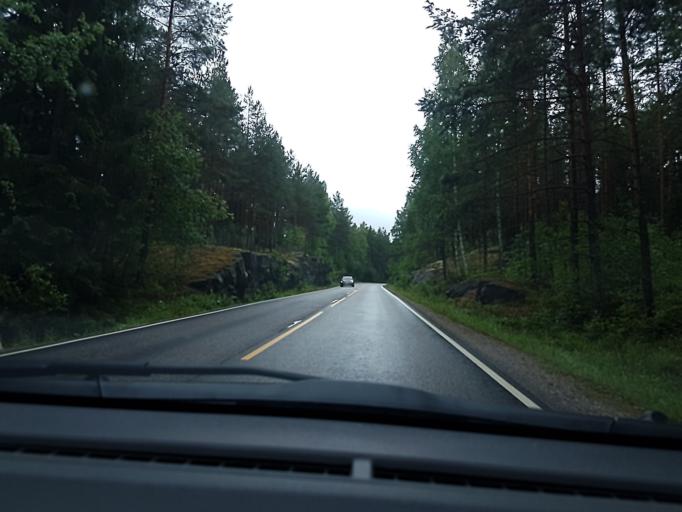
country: FI
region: Uusimaa
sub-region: Helsinki
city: Pornainen
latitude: 60.4611
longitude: 25.3890
